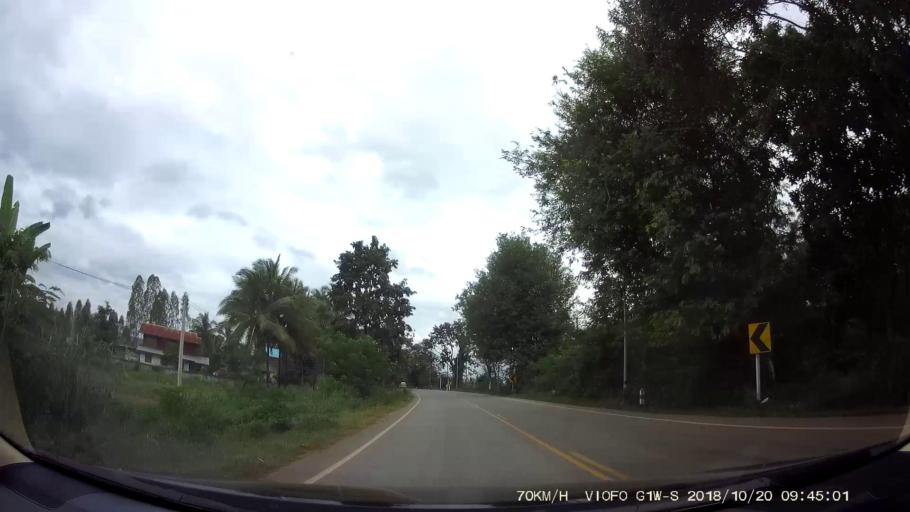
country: TH
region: Chaiyaphum
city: Khon San
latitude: 16.4888
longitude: 101.9409
